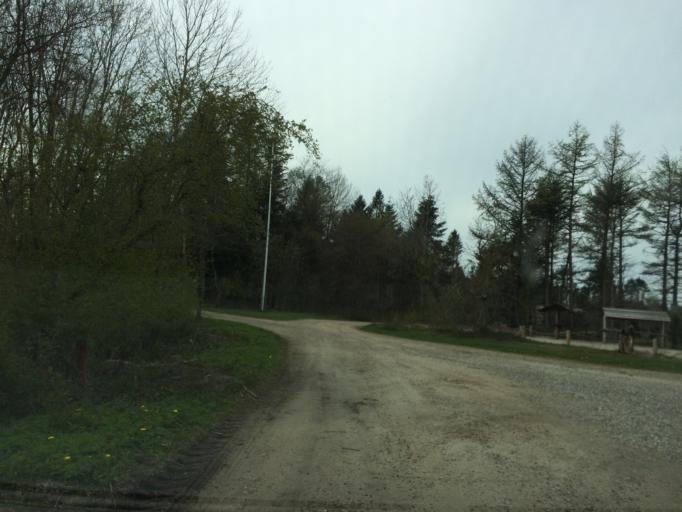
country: DK
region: Central Jutland
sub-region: Holstebro Kommune
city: Ulfborg
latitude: 56.2227
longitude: 8.4713
